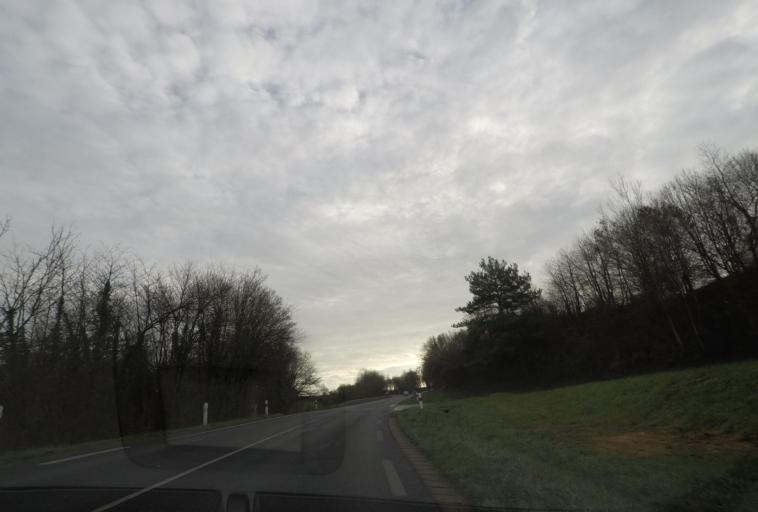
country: FR
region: Centre
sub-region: Departement du Loir-et-Cher
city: Sarge-sur-Braye
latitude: 47.9085
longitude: 0.8590
